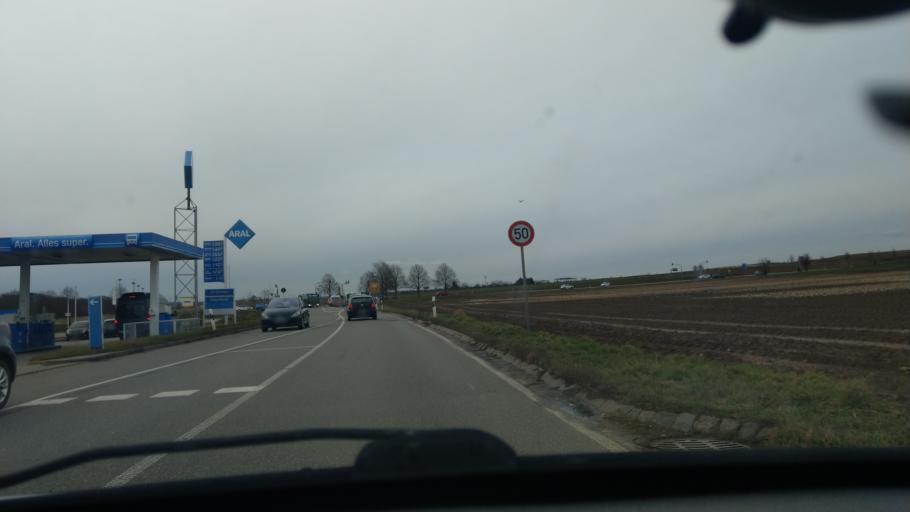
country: DE
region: Baden-Wuerttemberg
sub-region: Regierungsbezirk Stuttgart
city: Neuhausen auf den Fildern
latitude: 48.6914
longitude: 9.2669
